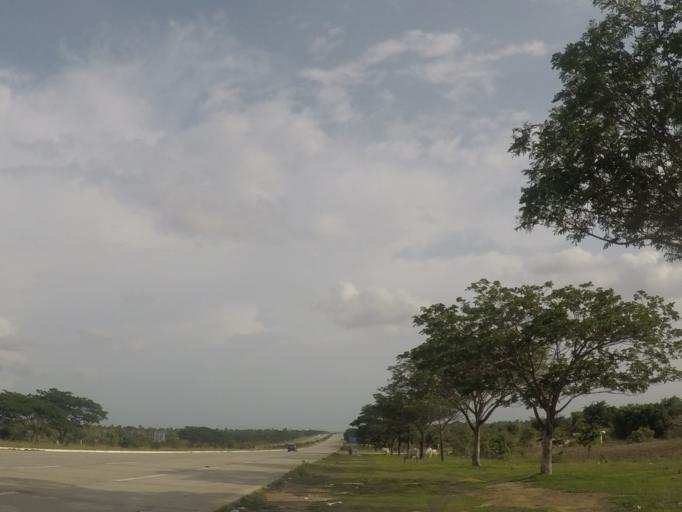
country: MM
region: Mandalay
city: Yamethin
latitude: 20.4967
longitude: 95.8248
